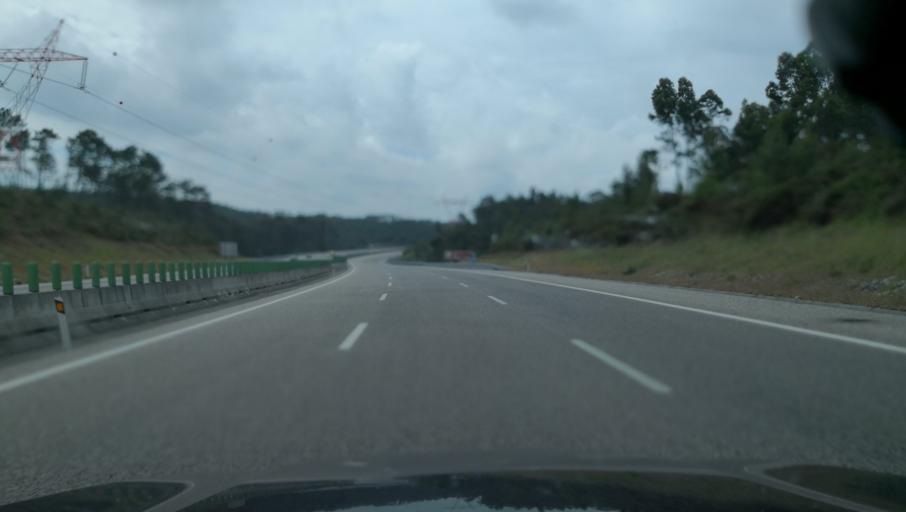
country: PT
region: Leiria
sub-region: Pombal
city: Lourical
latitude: 39.9555
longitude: -8.7739
